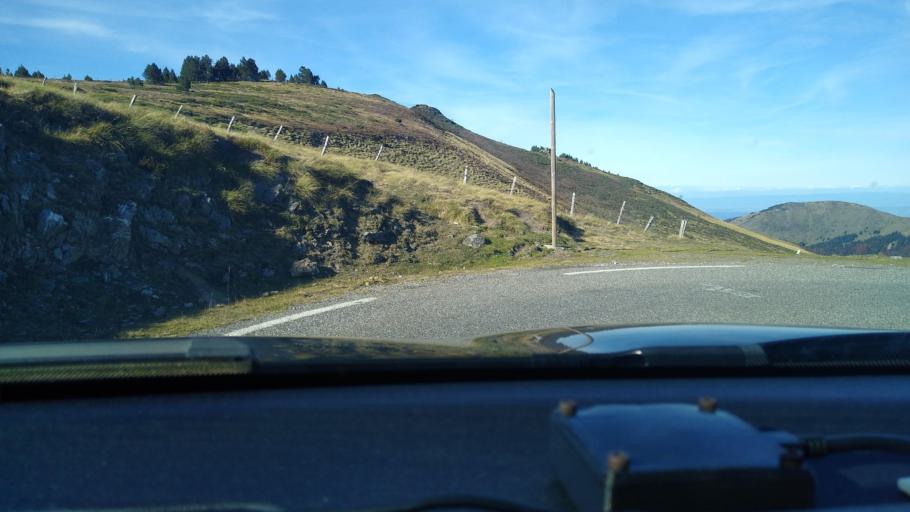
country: FR
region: Midi-Pyrenees
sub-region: Departement de l'Ariege
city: Ax-les-Thermes
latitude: 42.7362
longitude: 1.9991
